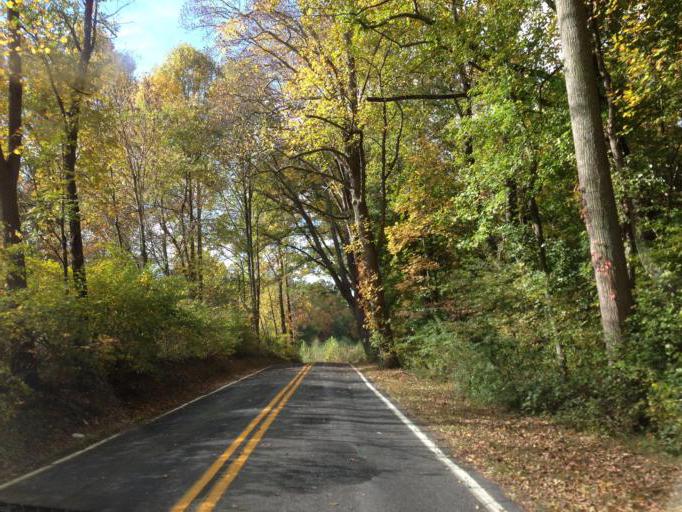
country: US
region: Maryland
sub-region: Carroll County
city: Mount Airy
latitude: 39.3142
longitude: -77.1331
